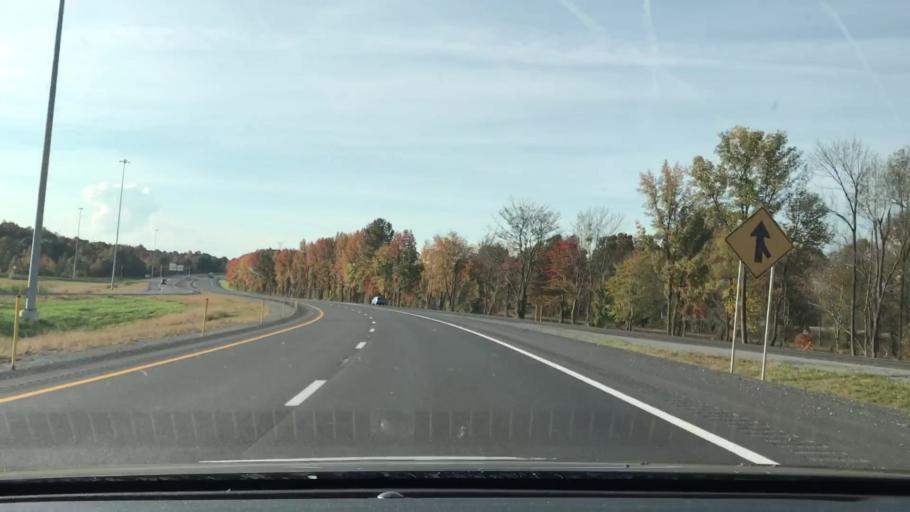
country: US
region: Kentucky
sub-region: Marshall County
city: Calvert City
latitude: 36.9861
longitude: -88.3463
